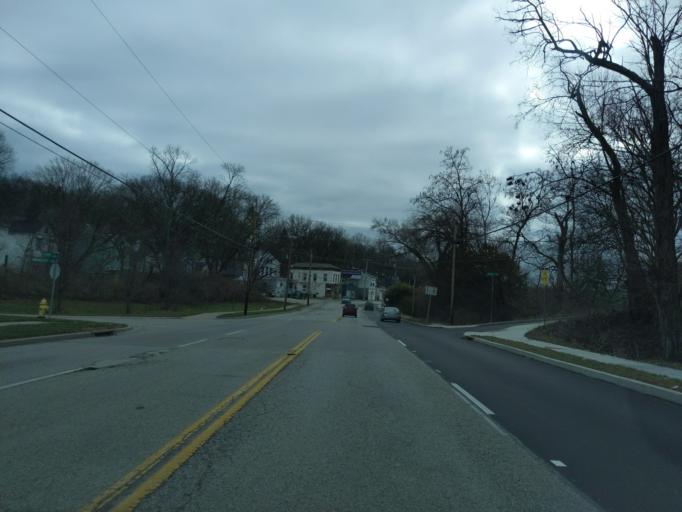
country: US
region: Ohio
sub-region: Hamilton County
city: Finneytown
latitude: 39.1729
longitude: -84.5474
